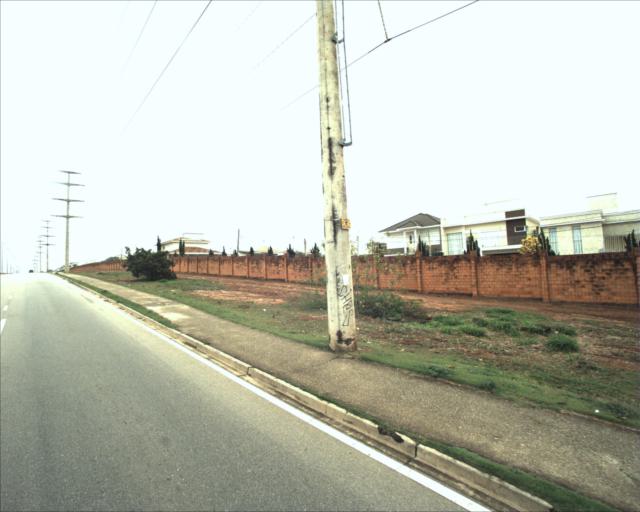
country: BR
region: Sao Paulo
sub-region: Sorocaba
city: Sorocaba
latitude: -23.4460
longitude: -47.4541
